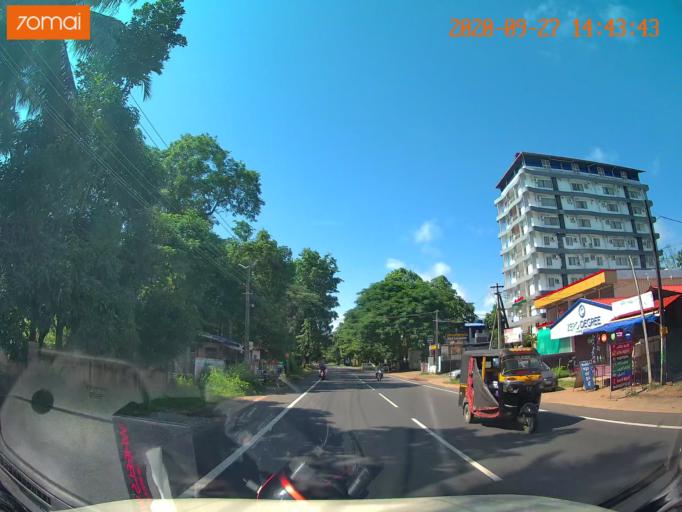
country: IN
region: Kerala
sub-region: Thrissur District
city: Thanniyam
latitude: 10.4448
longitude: 76.0924
